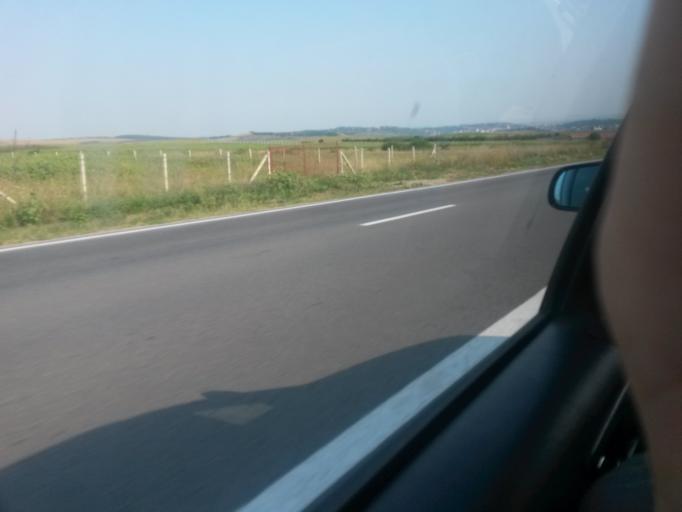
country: RO
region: Cluj
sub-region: Comuna Sandulesti
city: Copaceni
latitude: 46.6006
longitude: 23.7419
